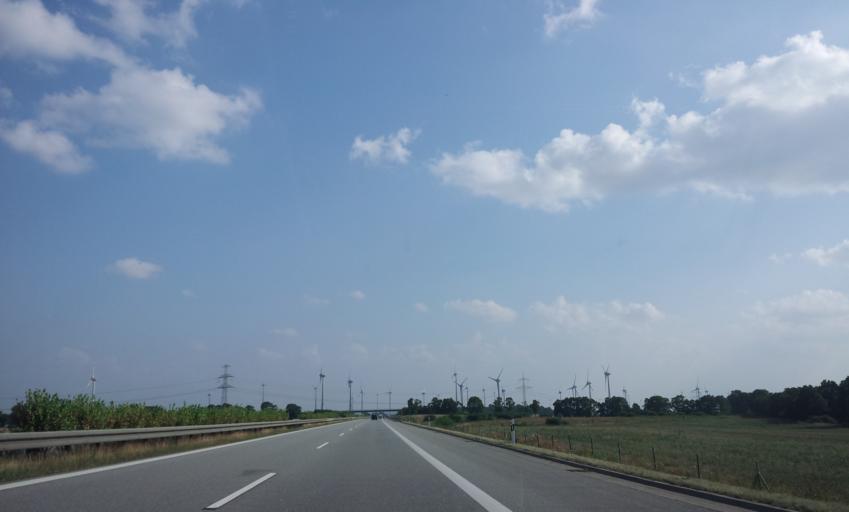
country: DE
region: Mecklenburg-Vorpommern
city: Kessin
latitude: 53.7550
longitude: 13.3334
